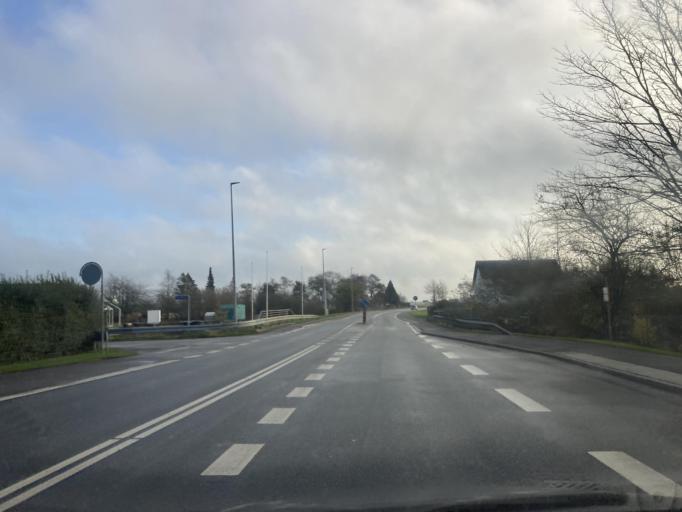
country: DK
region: Zealand
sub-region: Lolland Kommune
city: Maribo
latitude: 54.8043
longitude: 11.4398
